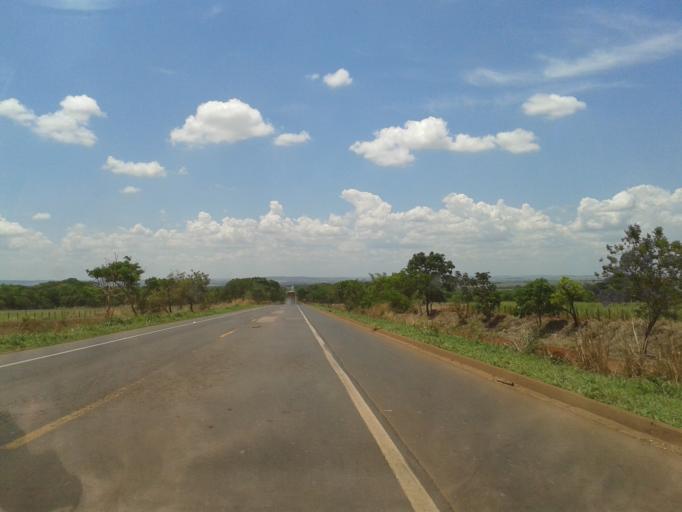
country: BR
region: Goias
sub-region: Goiatuba
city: Goiatuba
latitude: -18.2623
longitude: -49.6625
